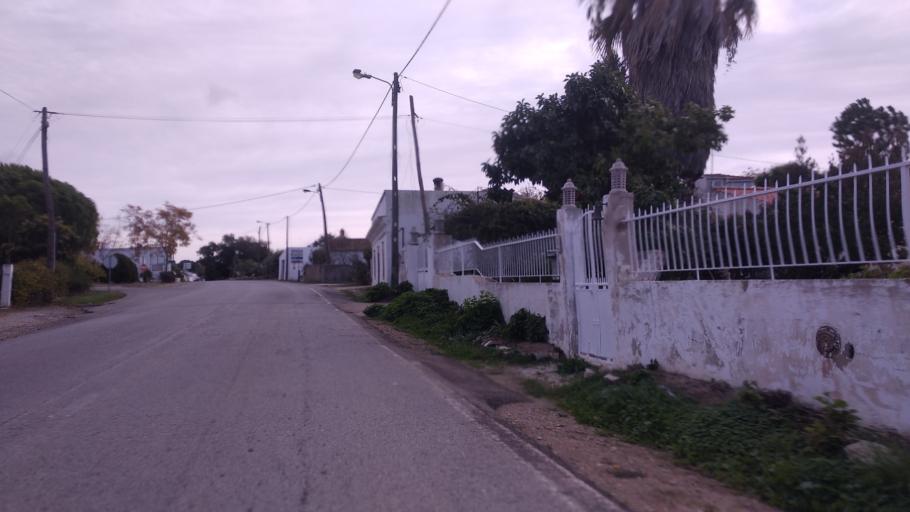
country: PT
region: Faro
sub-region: Sao Bras de Alportel
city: Sao Bras de Alportel
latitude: 37.1686
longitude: -7.9070
